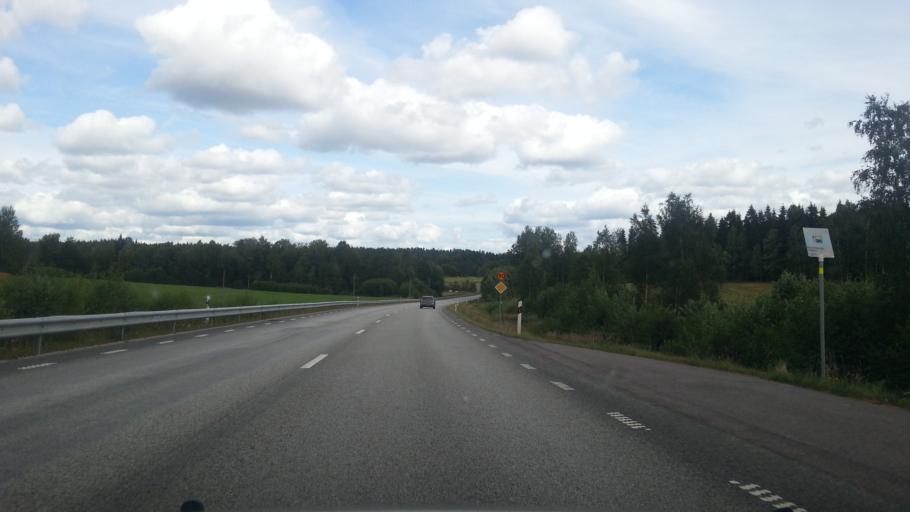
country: SE
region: OErebro
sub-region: Lindesbergs Kommun
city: Lindesberg
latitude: 59.6568
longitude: 15.2505
